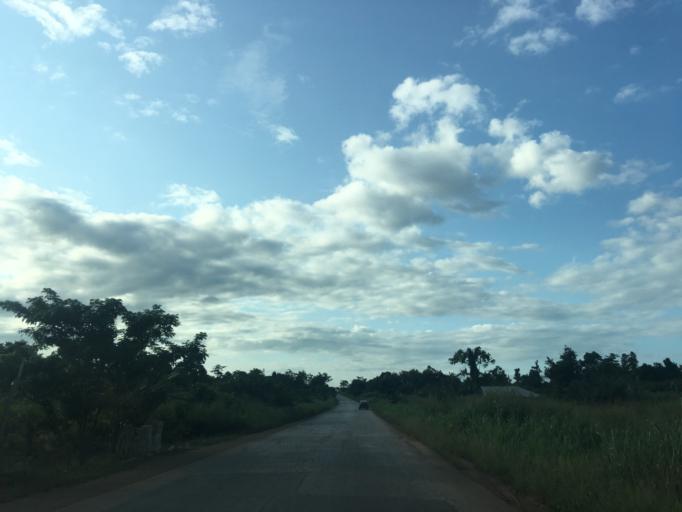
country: GH
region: Western
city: Bibiani
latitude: 6.3101
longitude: -2.2506
